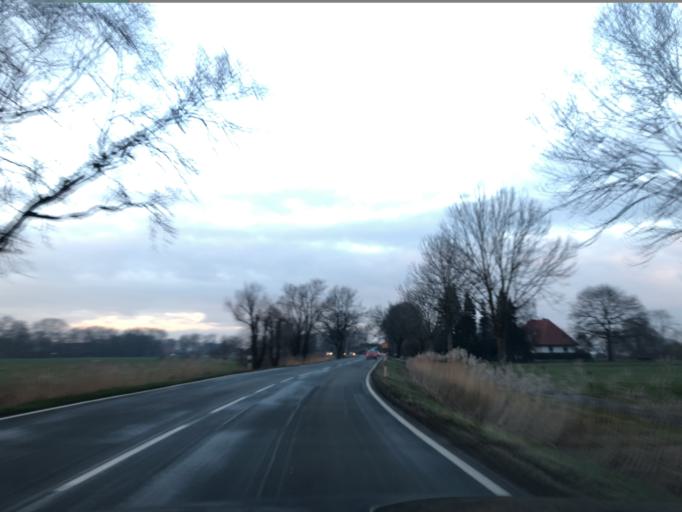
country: DE
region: Lower Saxony
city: Lemwerder
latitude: 53.1380
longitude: 8.5963
